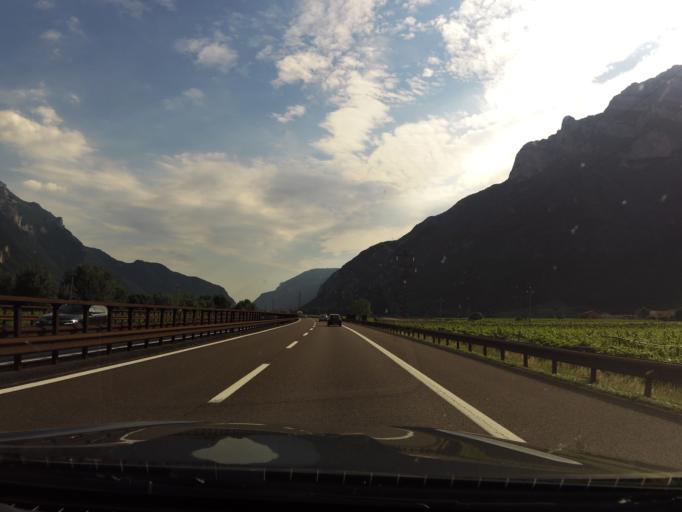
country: IT
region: Trentino-Alto Adige
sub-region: Provincia di Trento
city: Avio
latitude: 45.7297
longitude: 10.9427
